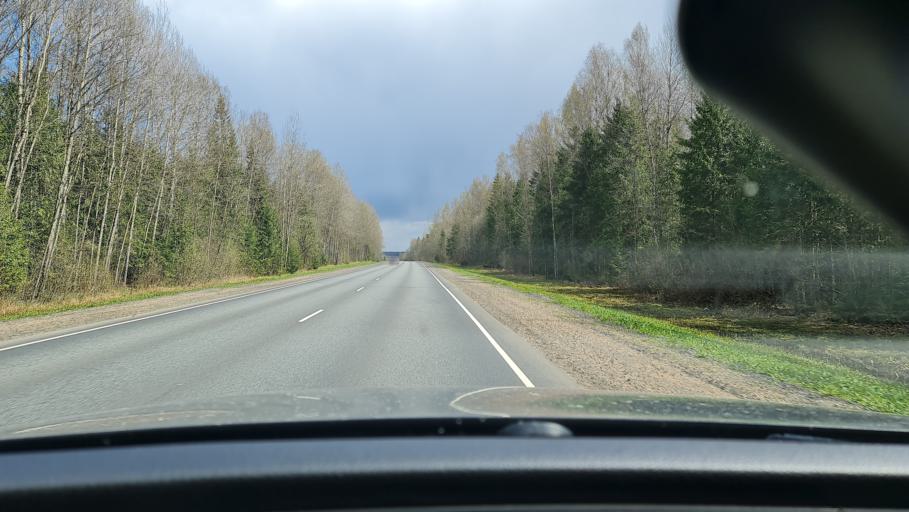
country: RU
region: Tverskaya
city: Zapadnaya Dvina
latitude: 56.3024
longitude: 32.3804
